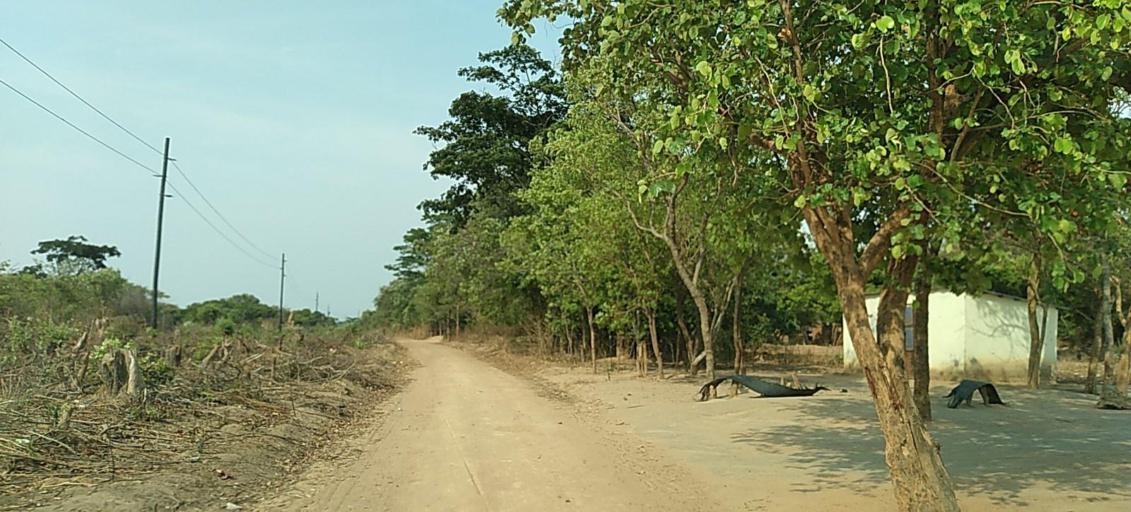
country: ZM
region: Copperbelt
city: Ndola
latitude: -13.2214
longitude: 28.6782
